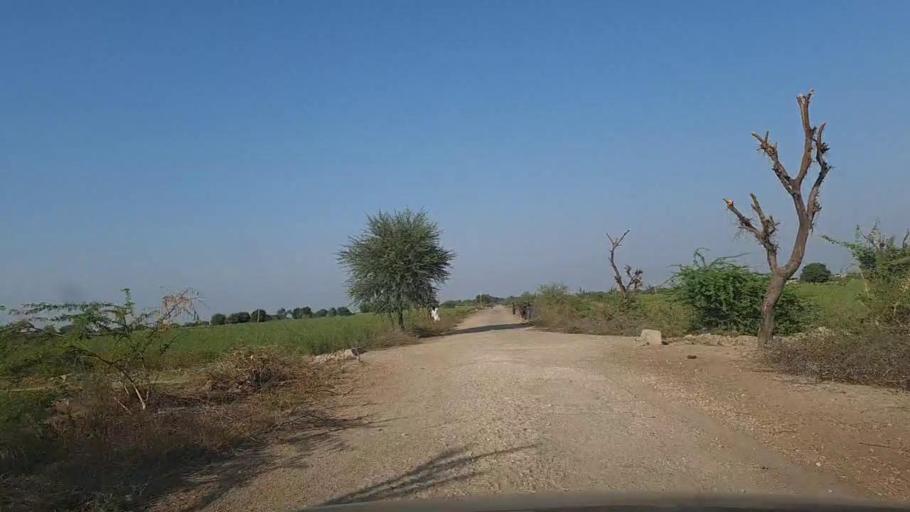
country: PK
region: Sindh
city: Digri
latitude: 25.0344
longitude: 69.2629
